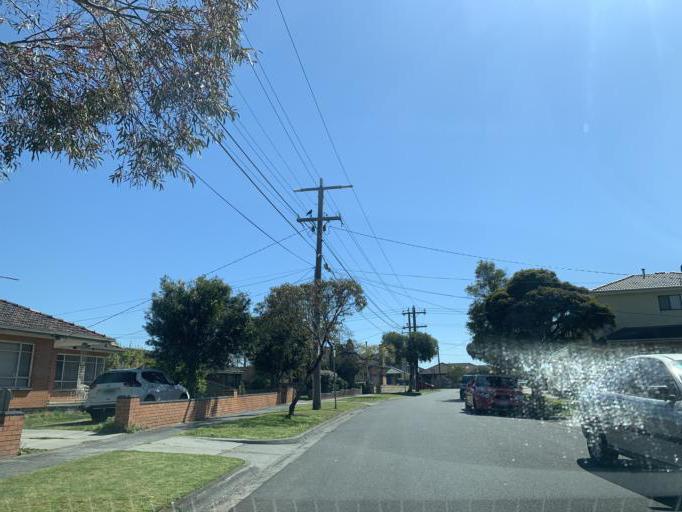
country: AU
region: Victoria
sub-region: Greater Dandenong
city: Dandenong
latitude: -38.0001
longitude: 145.2128
